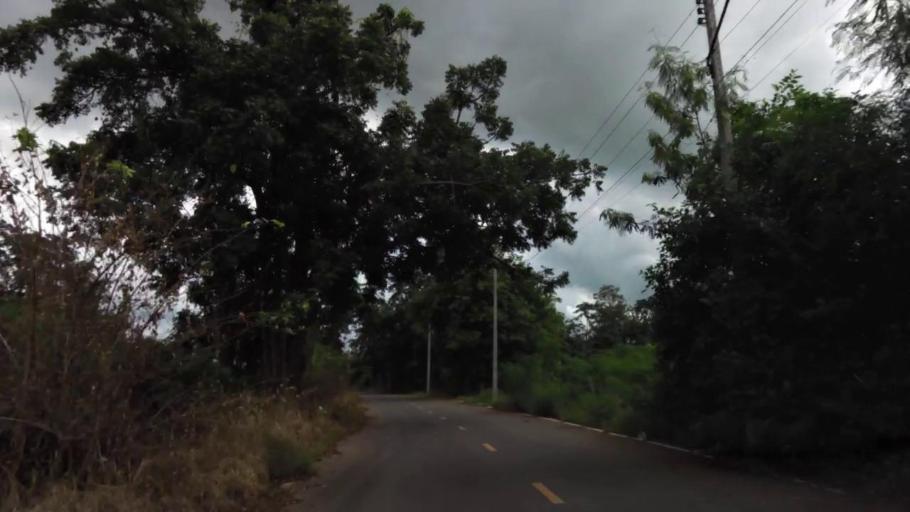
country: TH
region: Nakhon Sawan
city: Phai Sali
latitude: 15.6053
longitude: 100.6598
